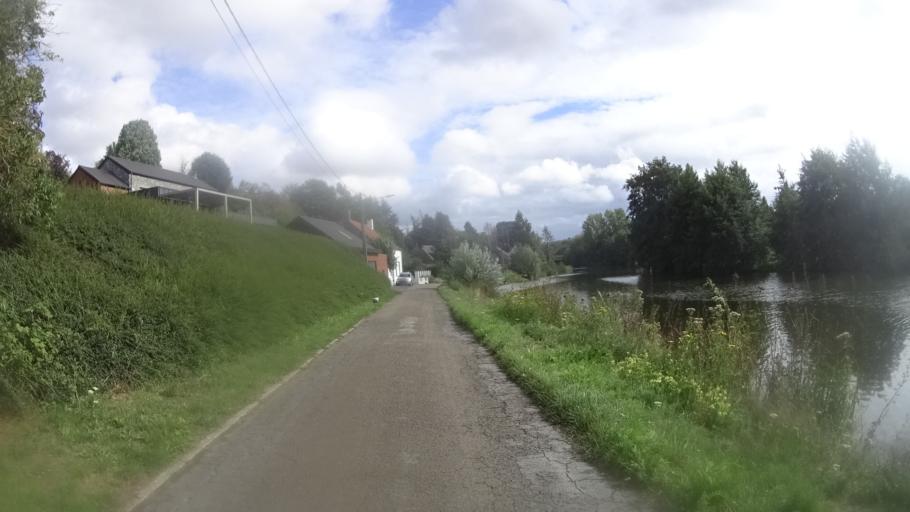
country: BE
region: Wallonia
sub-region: Province du Hainaut
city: Merbes-le-Chateau
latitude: 50.3187
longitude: 4.1801
